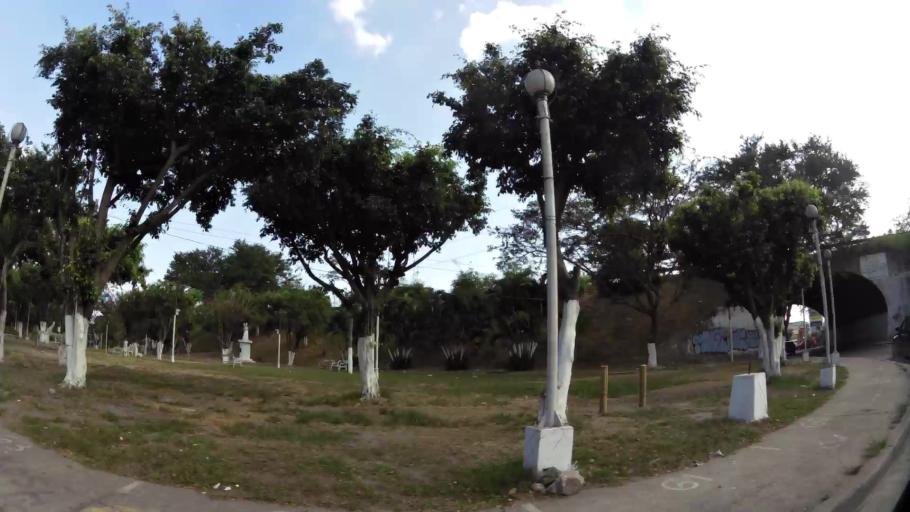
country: SV
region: San Salvador
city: Soyapango
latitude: 13.7162
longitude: -89.1420
